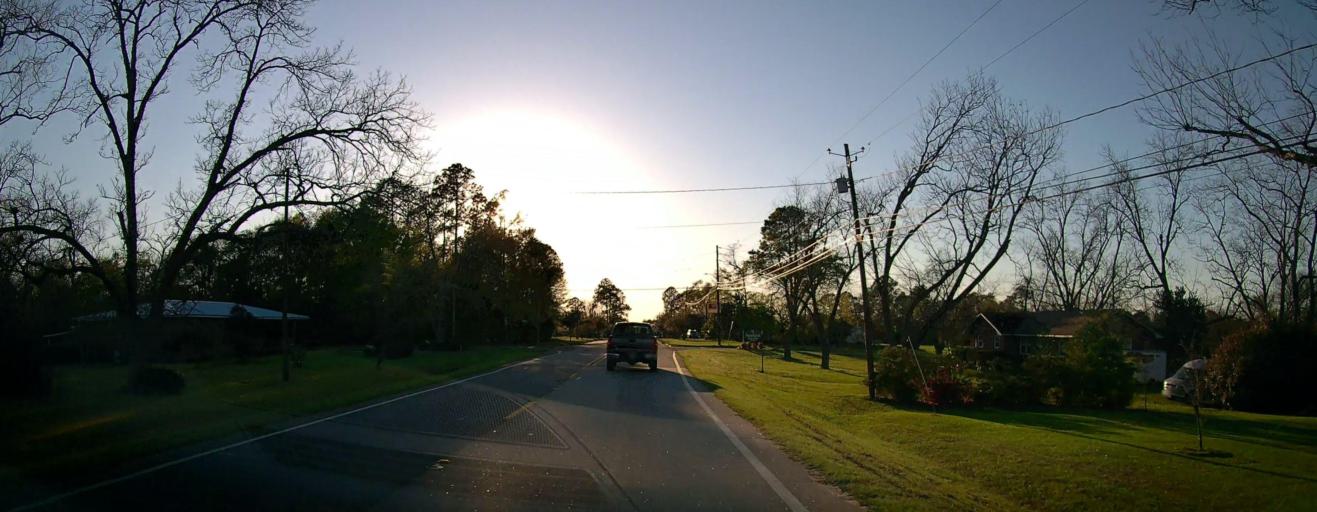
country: US
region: Georgia
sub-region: Wilcox County
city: Rochelle
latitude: 31.9508
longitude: -83.4458
